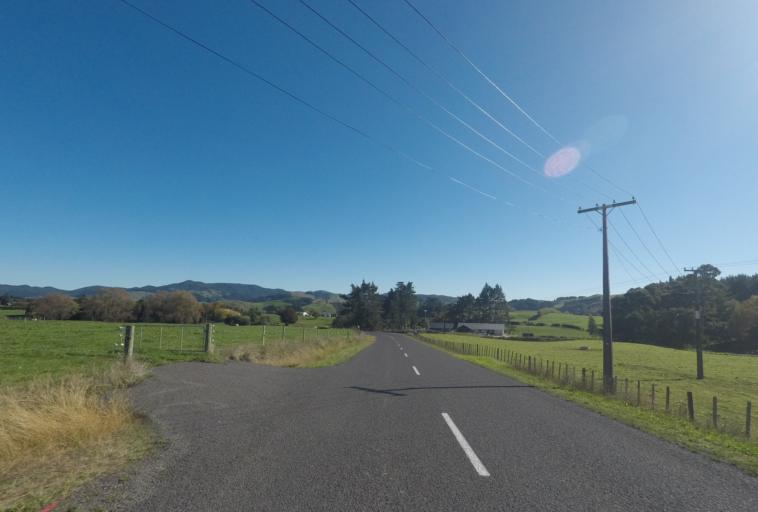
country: NZ
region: Bay of Plenty
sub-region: Western Bay of Plenty District
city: Waihi Beach
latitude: -37.3855
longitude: 175.8944
